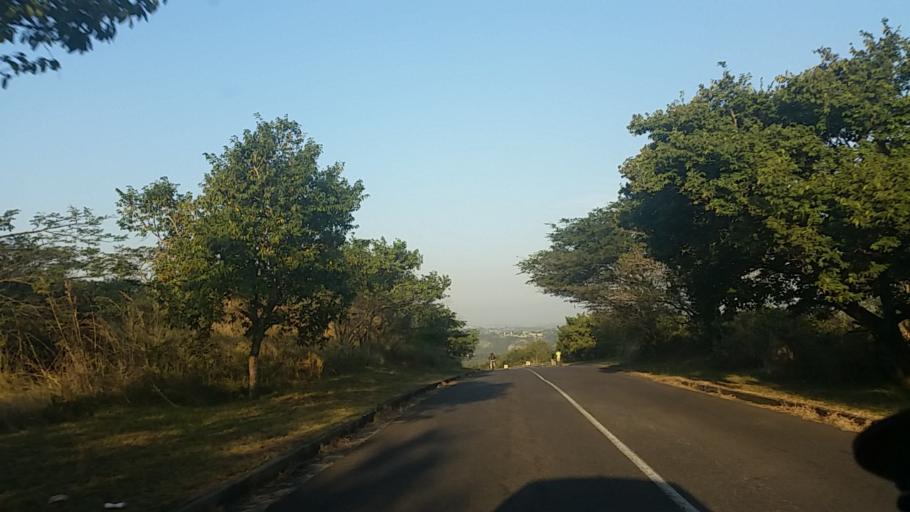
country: ZA
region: KwaZulu-Natal
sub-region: eThekwini Metropolitan Municipality
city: Berea
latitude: -29.8547
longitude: 30.9254
